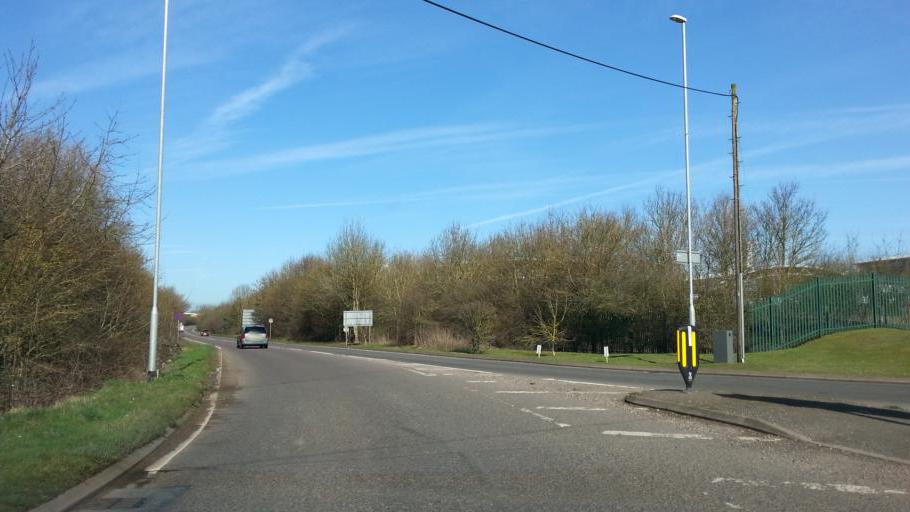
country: GB
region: England
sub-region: Northamptonshire
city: Brixworth
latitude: 52.3333
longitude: -0.8967
